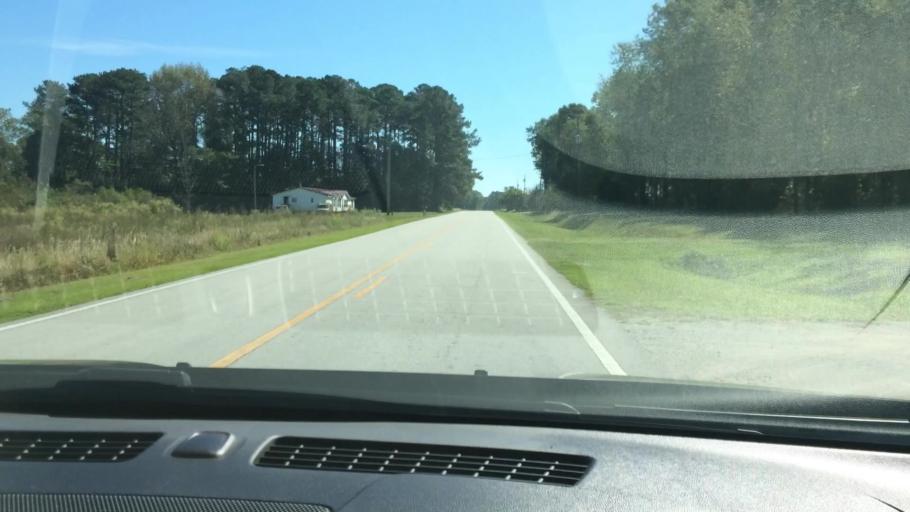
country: US
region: North Carolina
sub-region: Pitt County
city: Grifton
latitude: 35.3410
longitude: -77.3133
